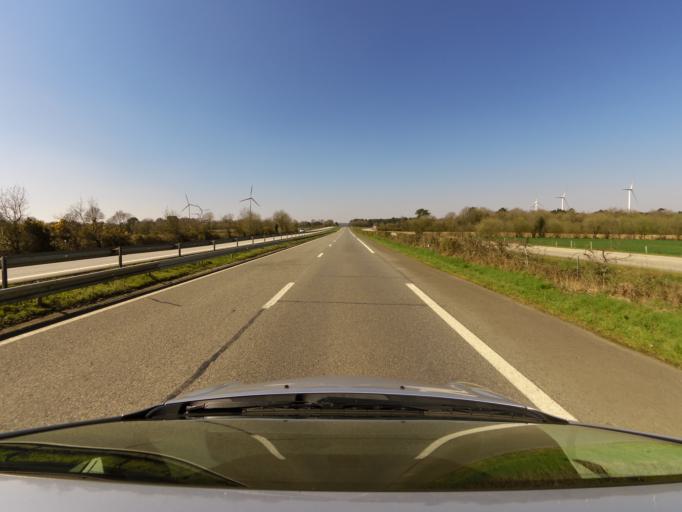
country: FR
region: Brittany
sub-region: Departement du Morbihan
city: Pleugriffet
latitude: 47.9234
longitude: -2.6907
